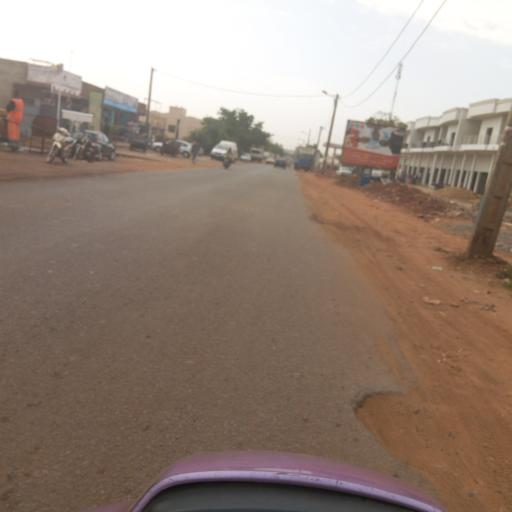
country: ML
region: Bamako
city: Bamako
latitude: 12.6563
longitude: -7.9362
